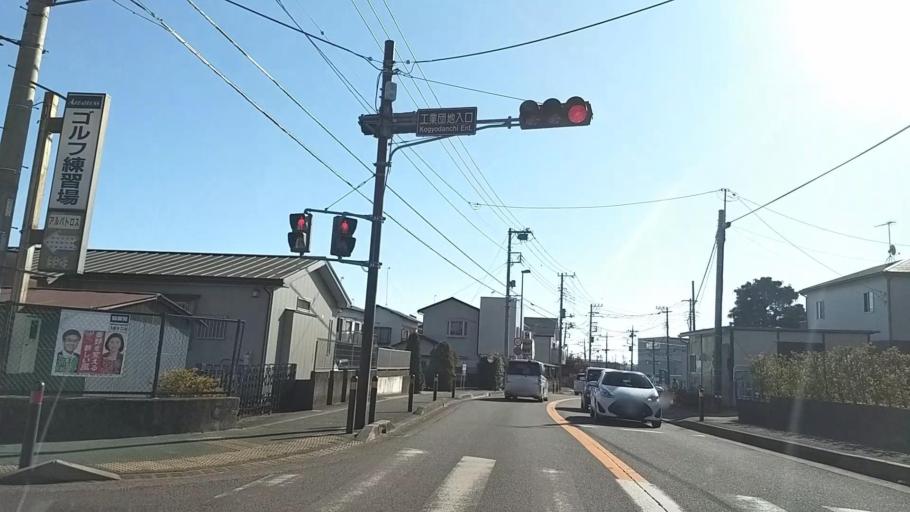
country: JP
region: Kanagawa
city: Hadano
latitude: 35.3944
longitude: 139.1978
